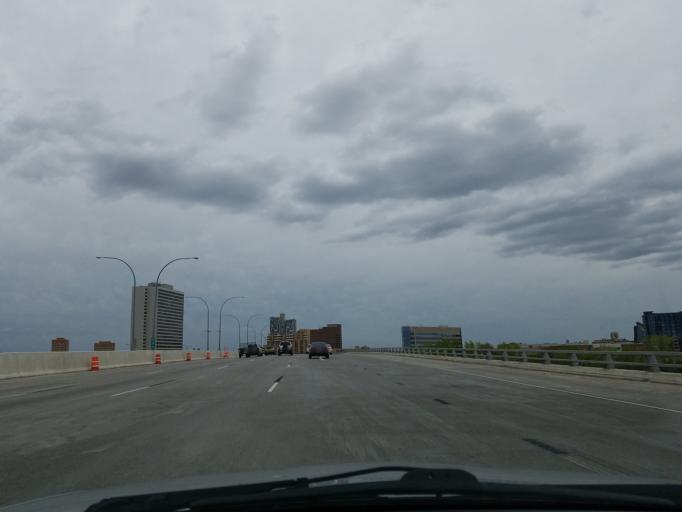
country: US
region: Minnesota
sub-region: Hennepin County
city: Minneapolis
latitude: 44.9801
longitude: -93.2448
